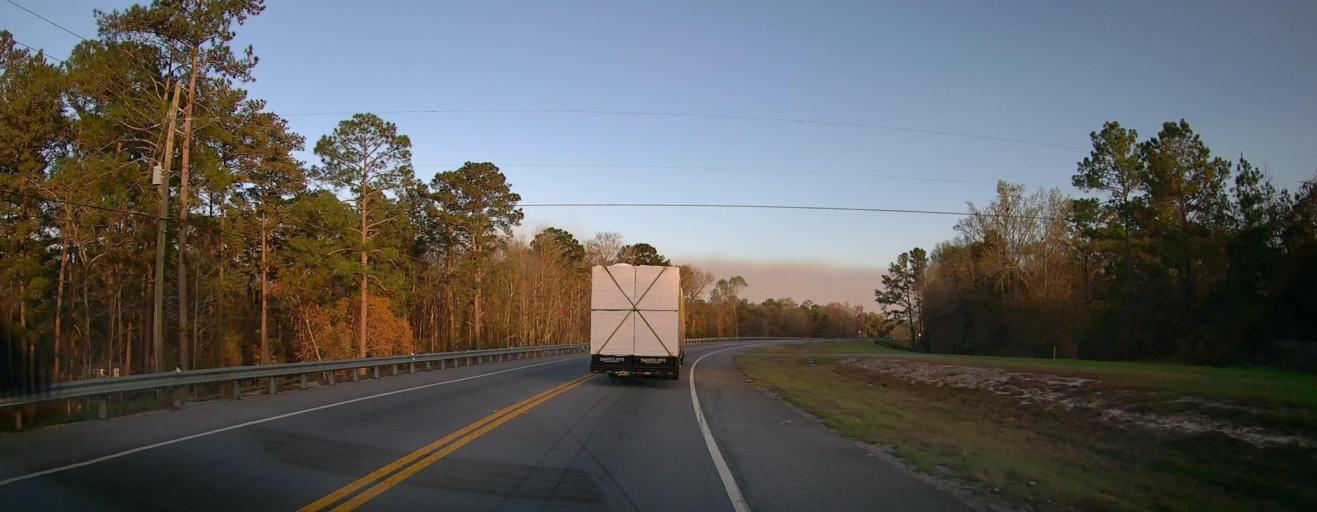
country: US
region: Georgia
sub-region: Chatham County
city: Bloomingdale
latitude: 32.1911
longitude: -81.4067
